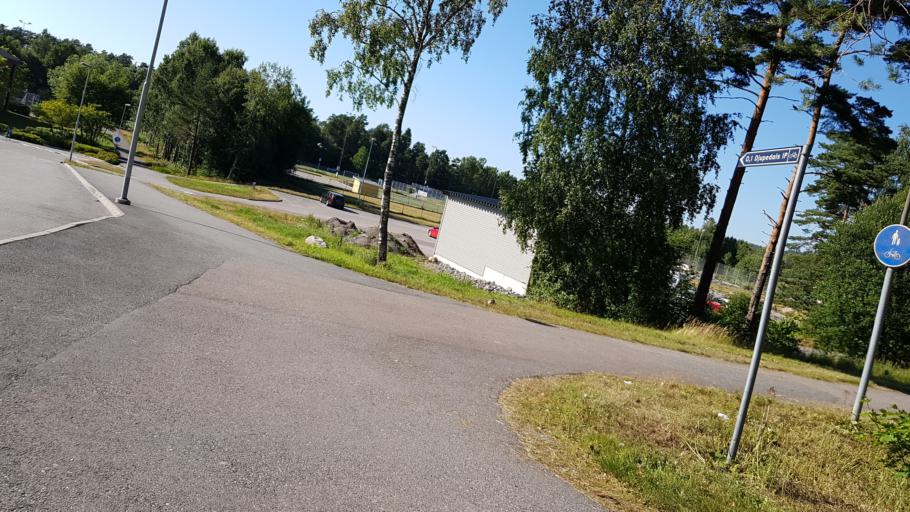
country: SE
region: Vaestra Goetaland
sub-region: Harryda Kommun
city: Molnlycke
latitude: 57.6514
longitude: 12.1280
